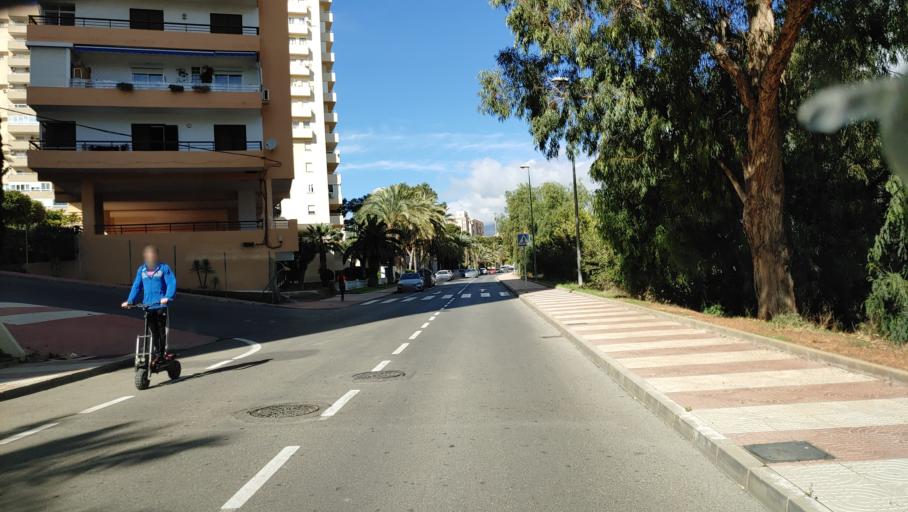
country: ES
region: Andalusia
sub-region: Provincia de Almeria
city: Aguadulce
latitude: 36.8103
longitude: -2.5764
